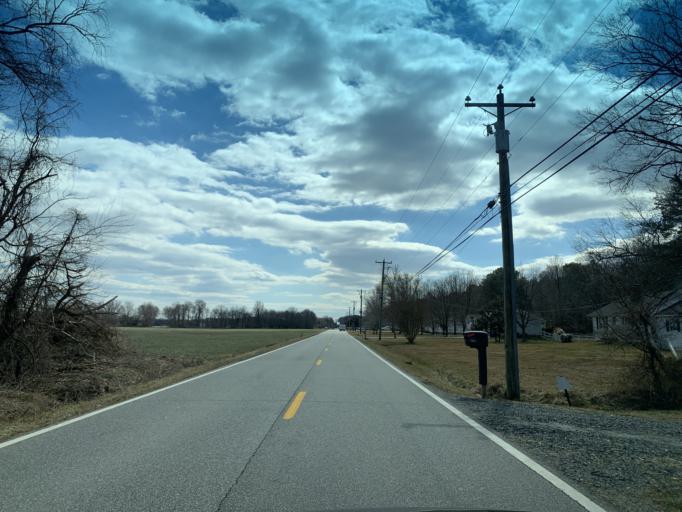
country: US
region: Maryland
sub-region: Queen Anne's County
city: Stevensville
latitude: 39.0150
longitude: -76.3114
